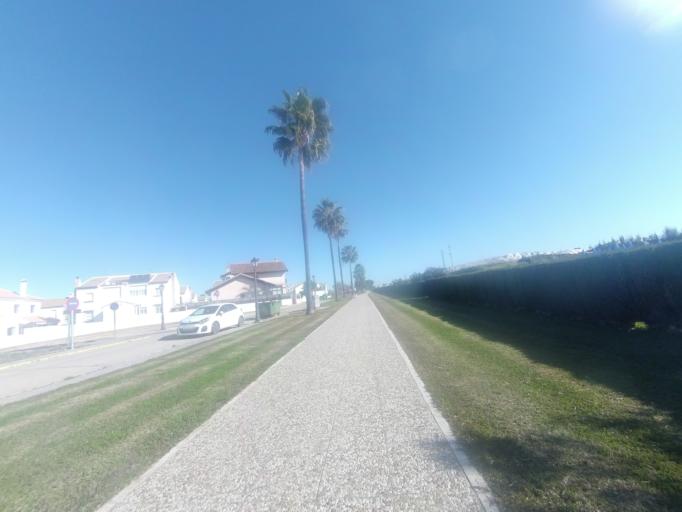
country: ES
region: Andalusia
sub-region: Provincia de Huelva
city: Palos de la Frontera
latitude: 37.2230
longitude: -6.9015
